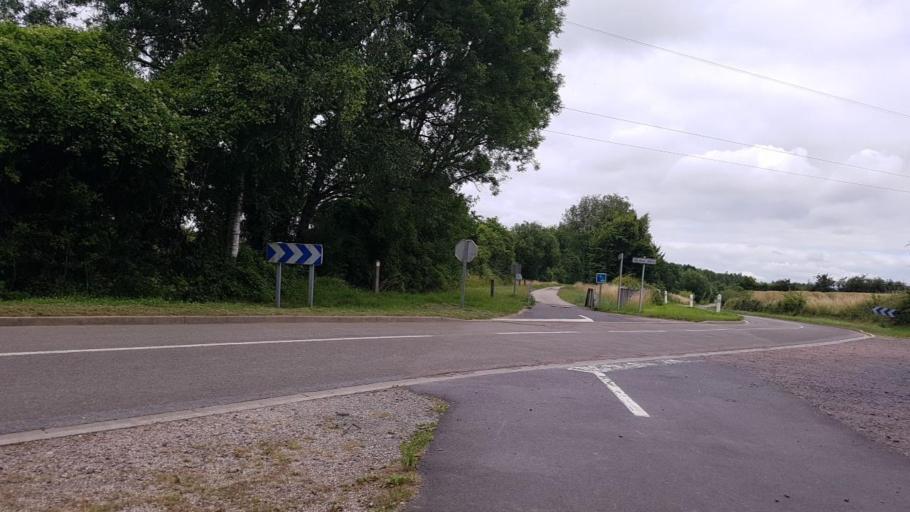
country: FR
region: Picardie
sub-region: Departement de l'Aisne
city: Origny-en-Thierache
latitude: 49.9261
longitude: 4.0411
